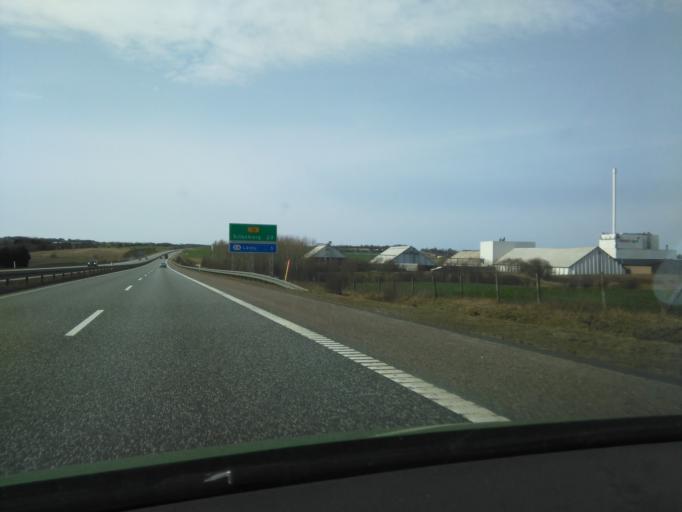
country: DK
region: Central Jutland
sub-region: Skanderborg Kommune
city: Galten
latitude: 56.1447
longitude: 9.9022
